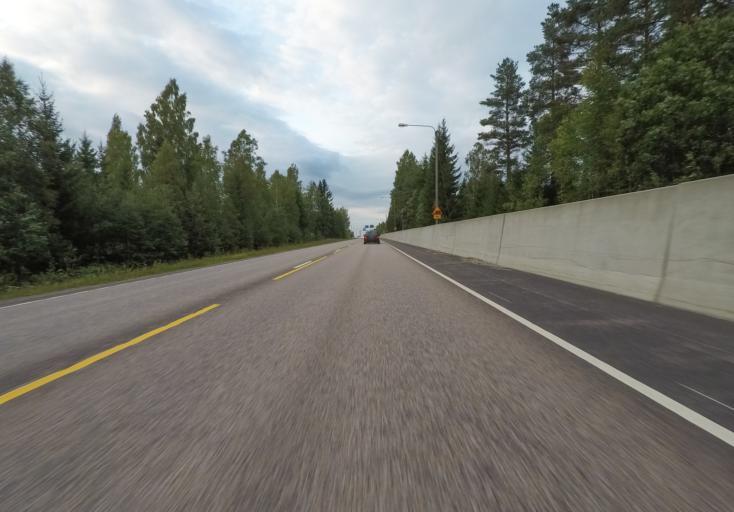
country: FI
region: Central Finland
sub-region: Joutsa
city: Joutsa
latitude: 61.7851
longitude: 26.0953
